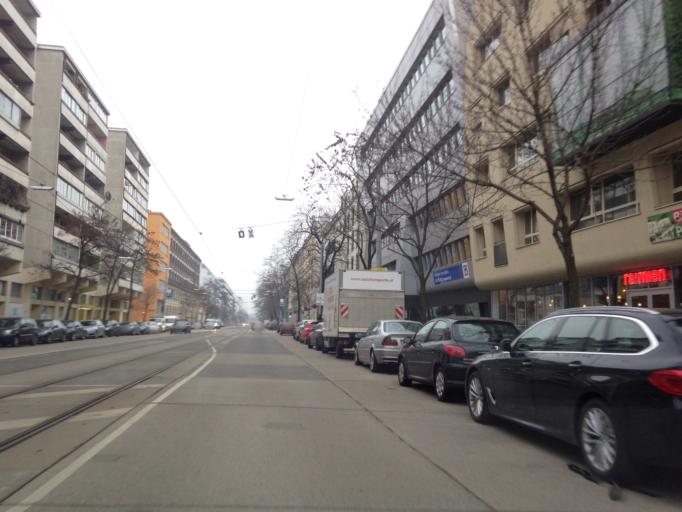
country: AT
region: Vienna
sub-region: Wien Stadt
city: Vienna
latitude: 48.2361
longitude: 16.3805
